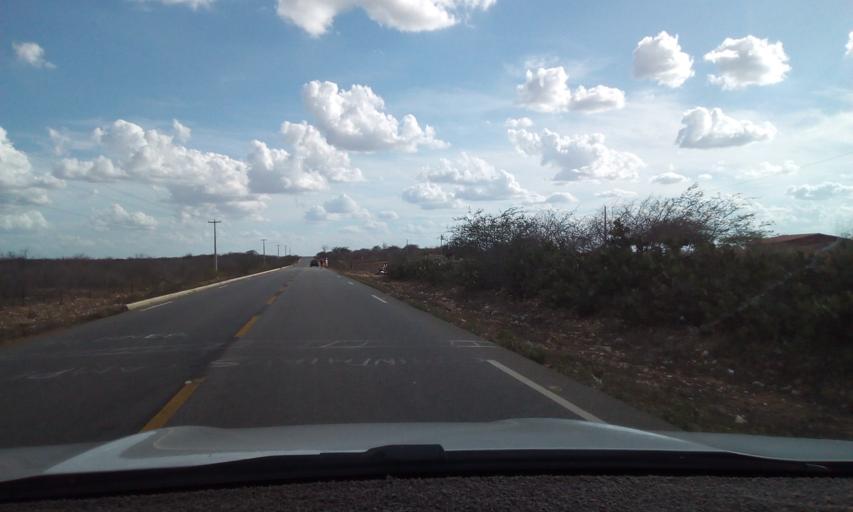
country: BR
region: Paraiba
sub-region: Soledade
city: Soledade
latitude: -6.8063
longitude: -36.4033
